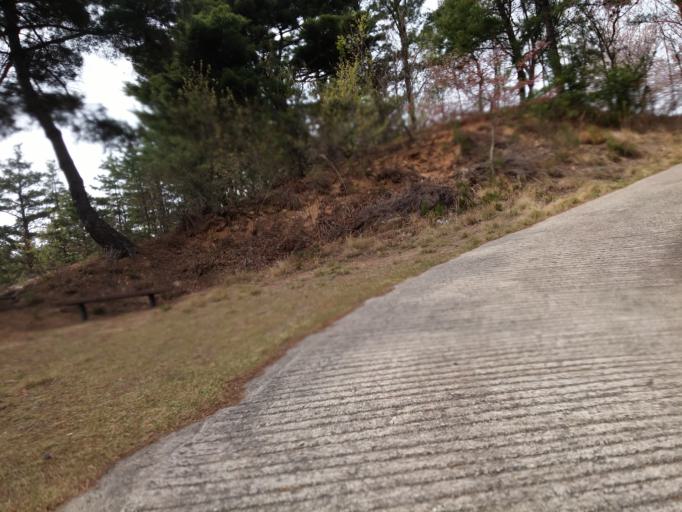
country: KR
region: Chungcheongbuk-do
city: Okcheon
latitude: 36.2509
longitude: 127.5570
